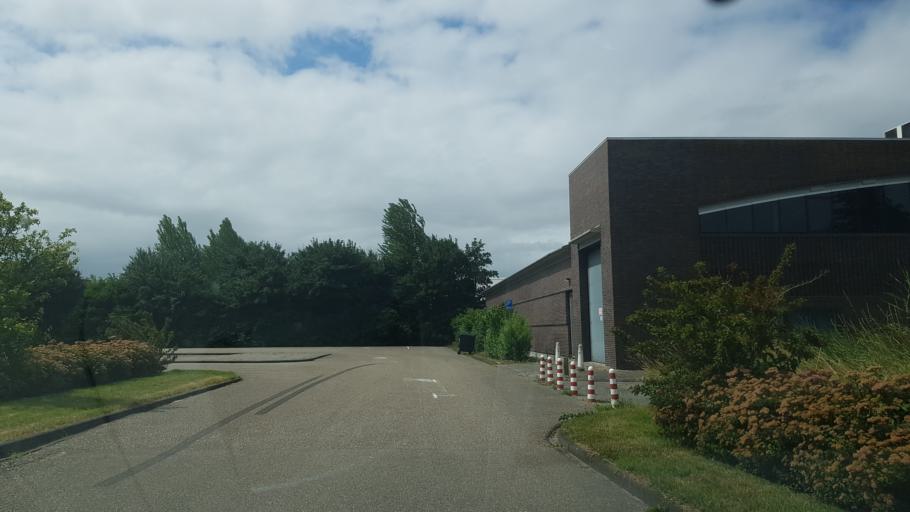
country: NL
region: North Holland
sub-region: Gemeente Enkhuizen
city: Enkhuizen
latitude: 52.6929
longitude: 5.2797
